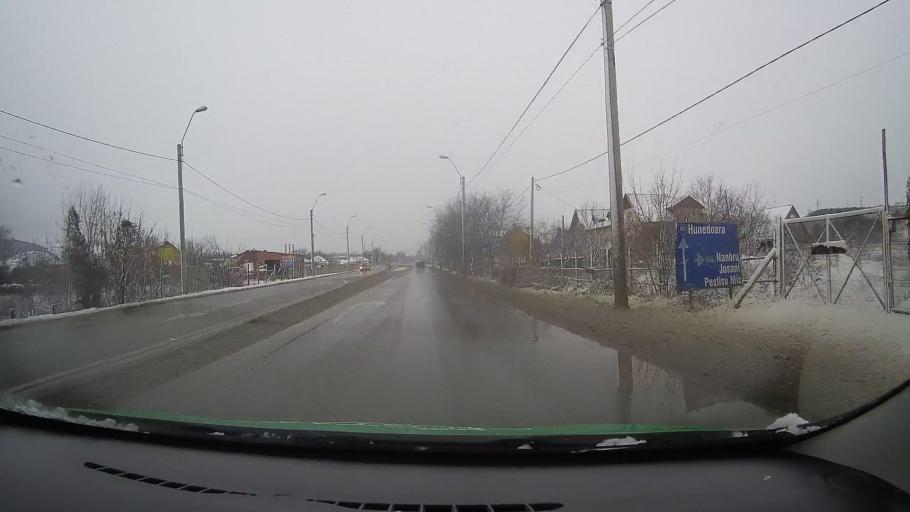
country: RO
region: Hunedoara
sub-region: Municipiul Hunedoara
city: Pestisu Mare
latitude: 45.8007
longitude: 22.9219
